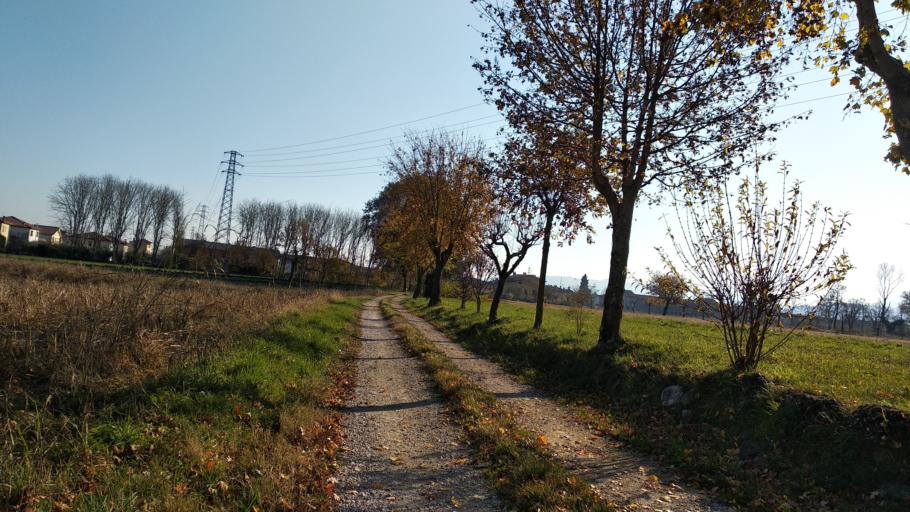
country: IT
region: Veneto
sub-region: Provincia di Vicenza
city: Schio
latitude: 45.7019
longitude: 11.3729
